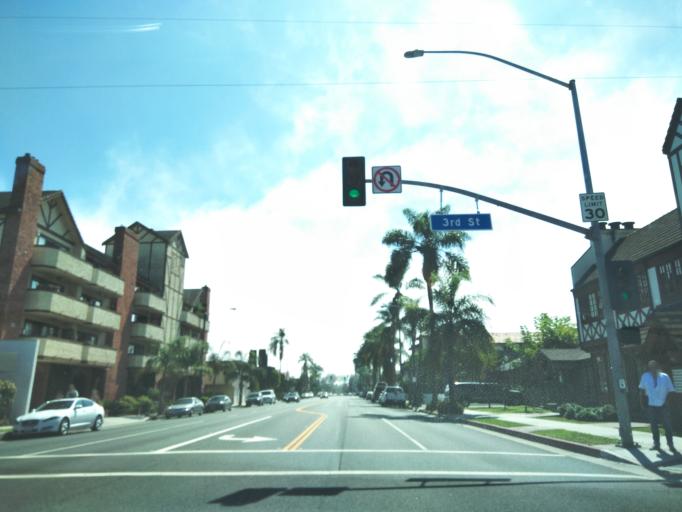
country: US
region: California
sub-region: Los Angeles County
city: Long Beach
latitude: 33.7681
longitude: -118.1525
